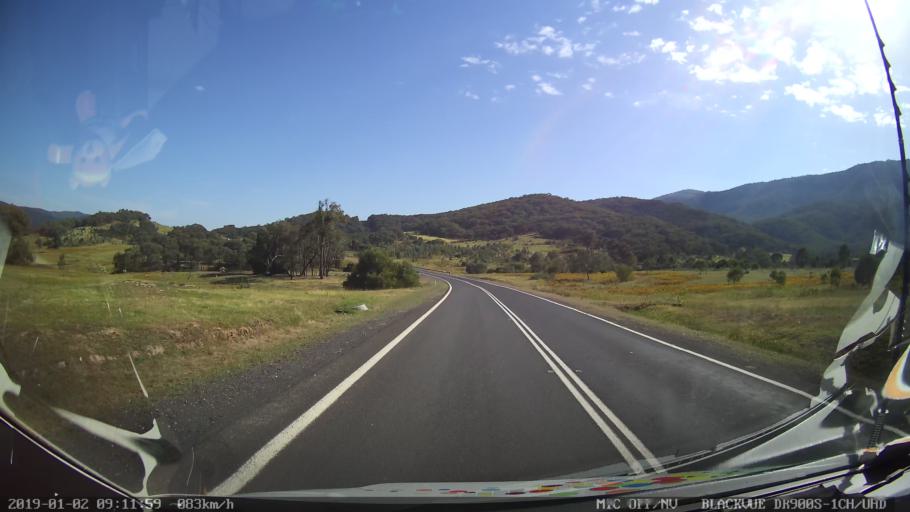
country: AU
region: New South Wales
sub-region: Tumut Shire
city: Tumut
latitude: -35.5059
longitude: 148.2719
